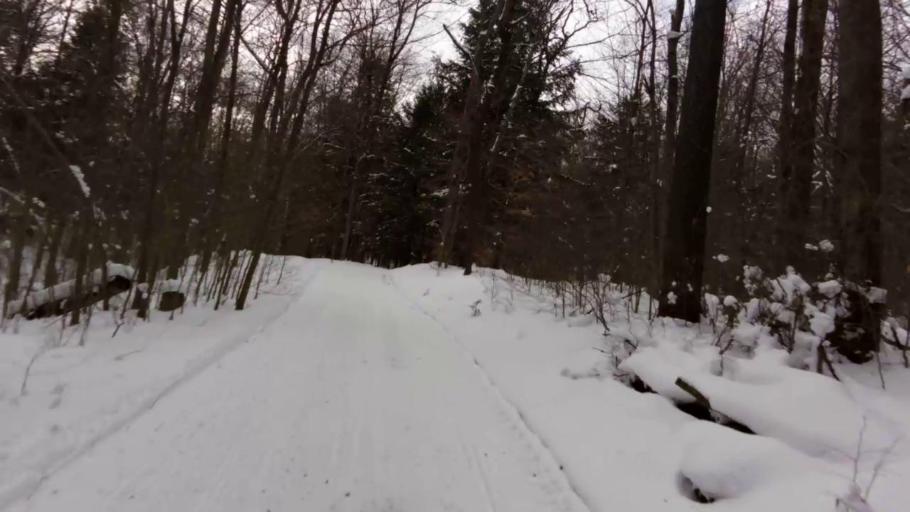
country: US
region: Pennsylvania
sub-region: McKean County
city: Bradford
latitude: 42.0276
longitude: -78.7271
